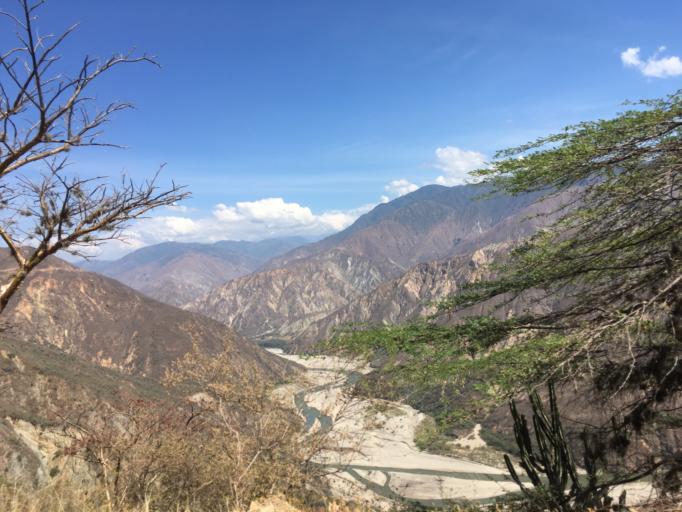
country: CO
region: Santander
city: Aratoca
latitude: 6.7710
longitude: -72.9905
